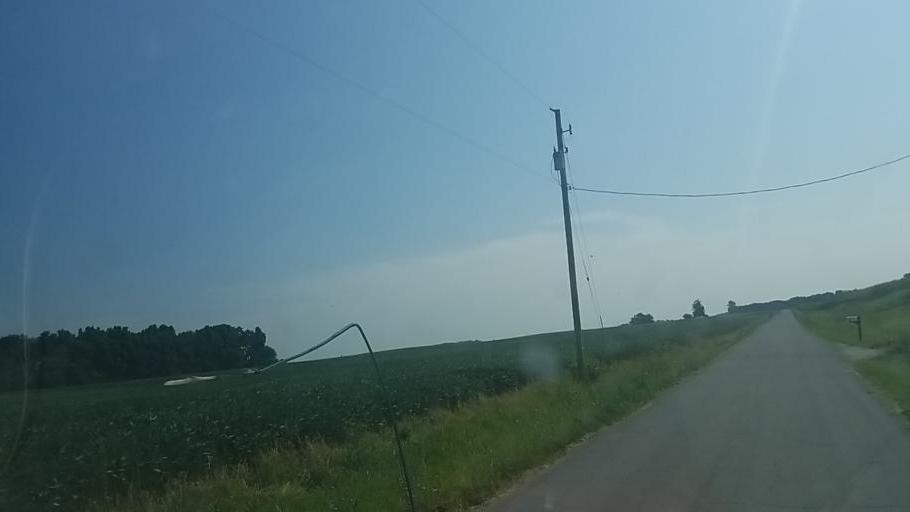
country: US
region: Ohio
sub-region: Marion County
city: Marion
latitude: 40.7170
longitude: -83.1577
